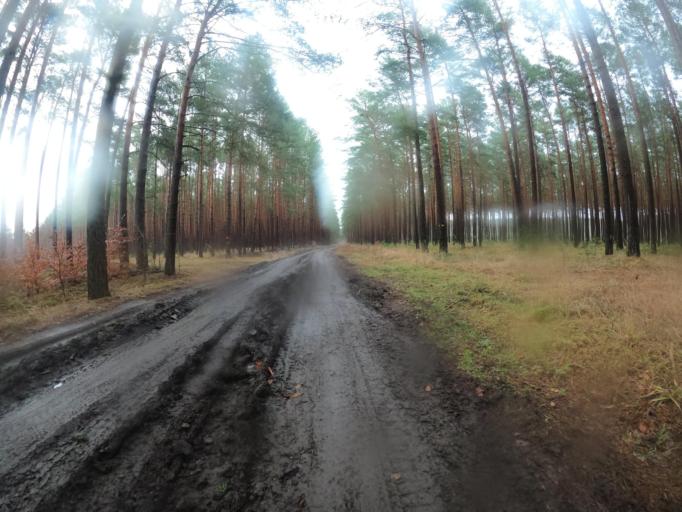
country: PL
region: Lubusz
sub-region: Powiat slubicki
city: Cybinka
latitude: 52.1877
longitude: 14.8939
